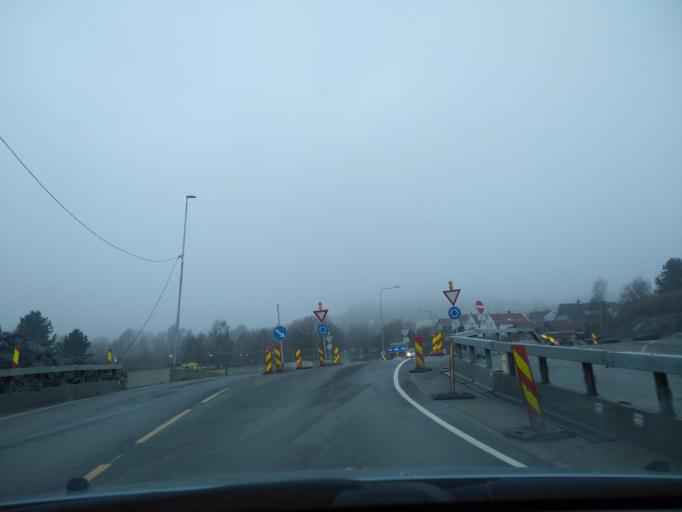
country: NO
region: Rogaland
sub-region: Stavanger
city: Stavanger
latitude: 58.9797
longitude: 5.6839
